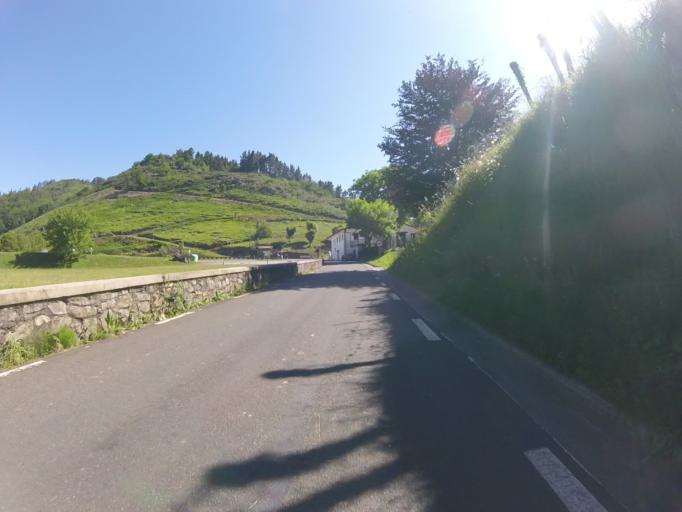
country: ES
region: Basque Country
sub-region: Provincia de Guipuzcoa
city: Albiztur
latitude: 43.1212
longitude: -2.1531
